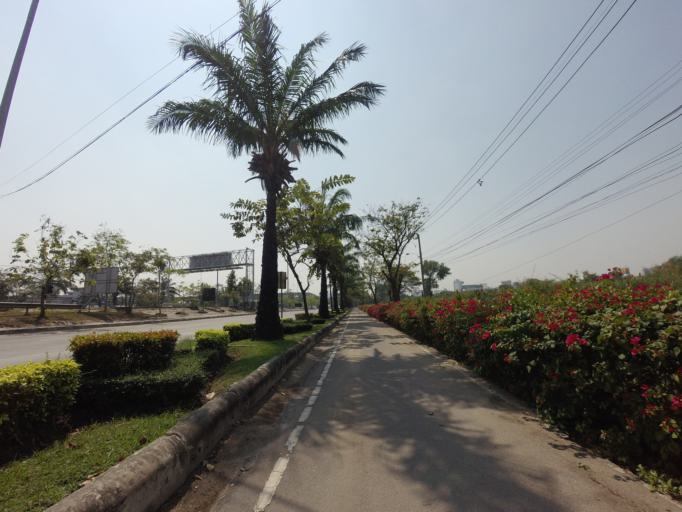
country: TH
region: Bangkok
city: Huai Khwang
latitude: 13.7553
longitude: 100.5945
